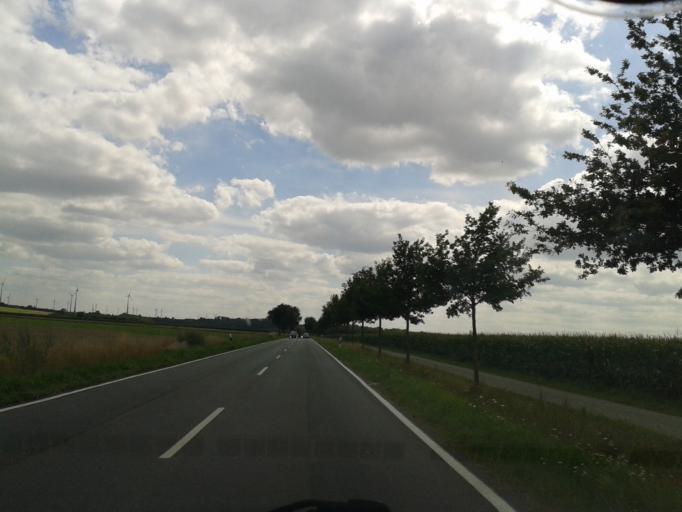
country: DE
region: North Rhine-Westphalia
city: Bad Lippspringe
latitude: 51.7670
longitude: 8.8368
